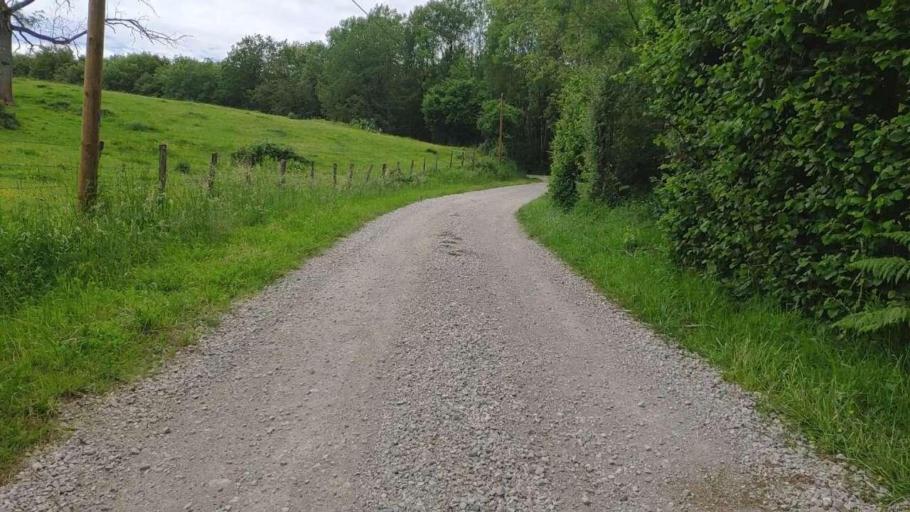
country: FR
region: Franche-Comte
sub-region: Departement du Jura
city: Montmorot
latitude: 46.7509
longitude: 5.5525
